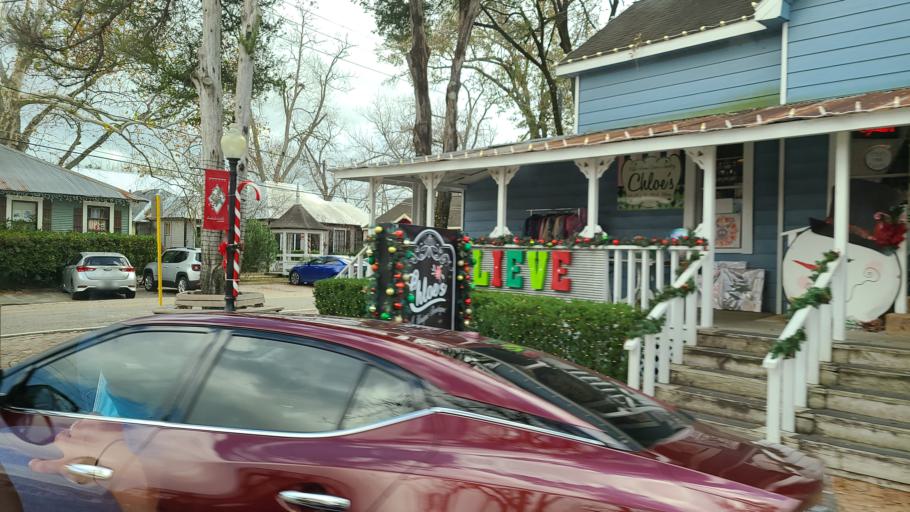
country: US
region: Texas
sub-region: Harris County
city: Spring
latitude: 30.0787
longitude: -95.4187
